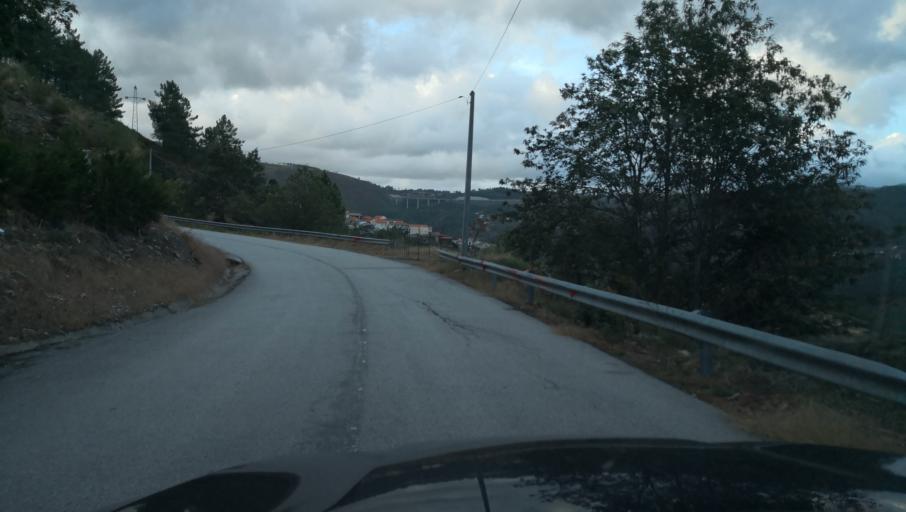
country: PT
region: Vila Real
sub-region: Santa Marta de Penaguiao
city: Santa Marta de Penaguiao
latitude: 41.2545
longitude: -7.8561
